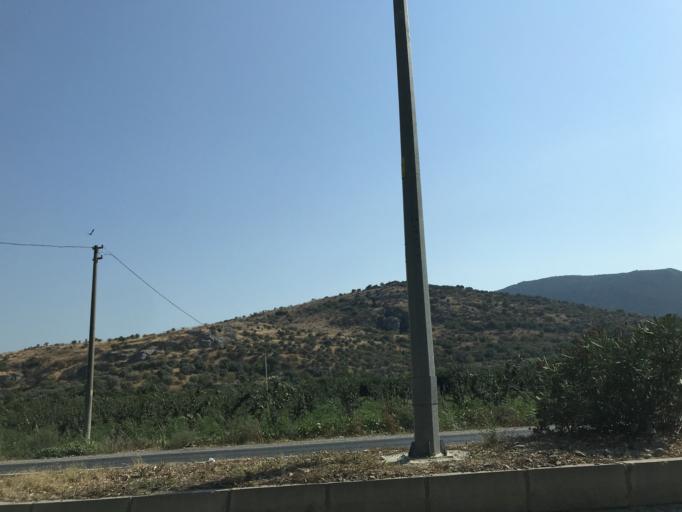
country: TR
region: Izmir
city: Selcuk
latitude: 37.9501
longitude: 27.3515
